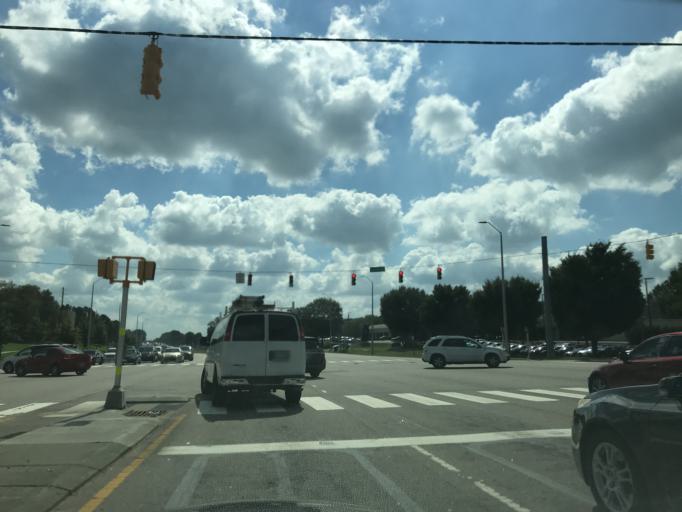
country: US
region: North Carolina
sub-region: Wake County
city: Raleigh
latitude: 35.8668
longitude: -78.5821
